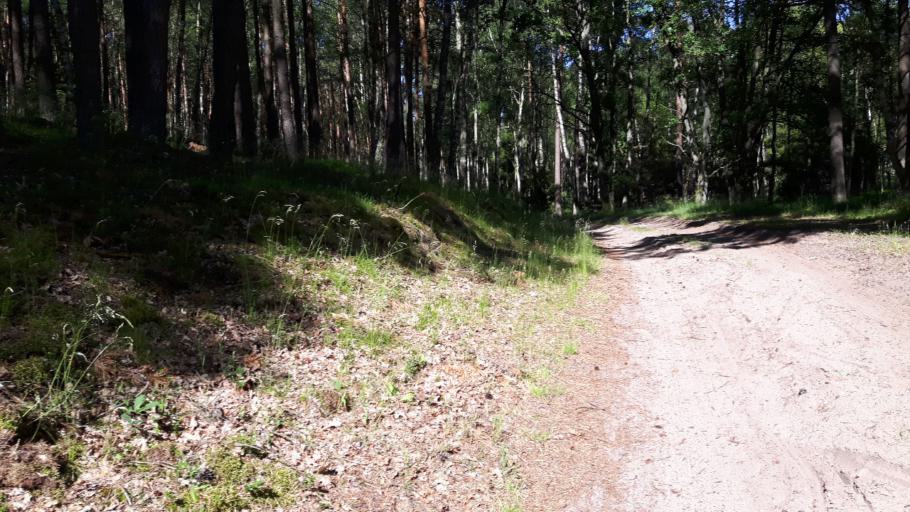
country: PL
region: Pomeranian Voivodeship
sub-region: Powiat leborski
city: Leba
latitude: 54.6994
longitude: 17.5022
